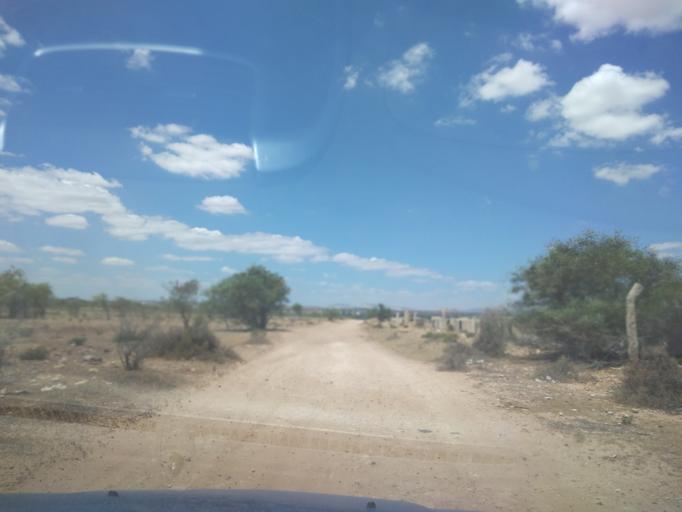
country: TN
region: Susah
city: Harqalah
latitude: 36.1667
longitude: 10.4406
